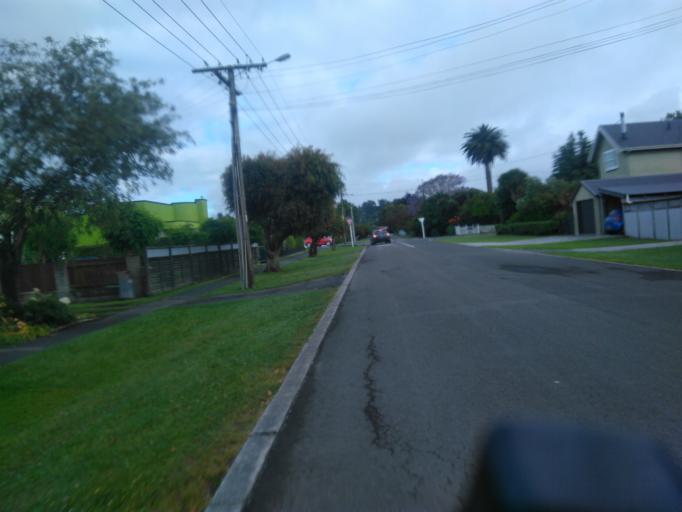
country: NZ
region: Gisborne
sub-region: Gisborne District
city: Gisborne
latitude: -38.6590
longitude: 178.0319
